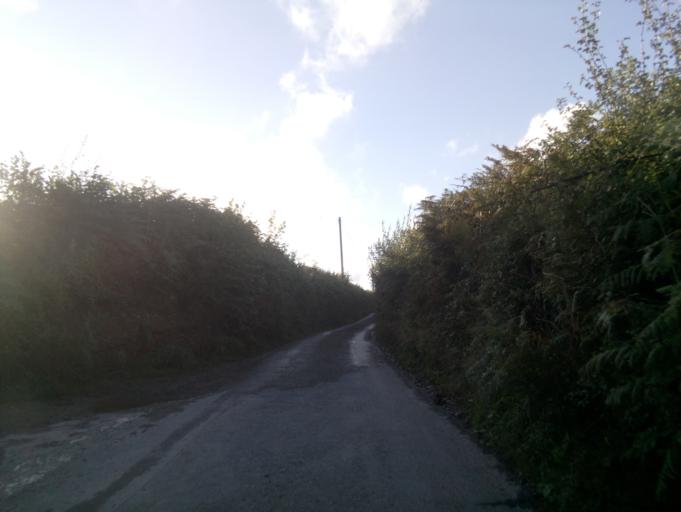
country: GB
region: England
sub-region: Devon
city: Dartmouth
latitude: 50.3412
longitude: -3.6078
